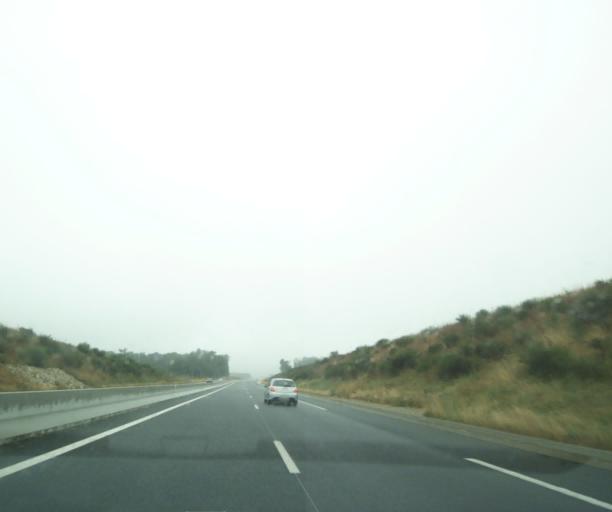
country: FR
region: Midi-Pyrenees
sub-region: Departement de l'Aveyron
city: Naucelle
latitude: 44.1966
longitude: 2.3760
